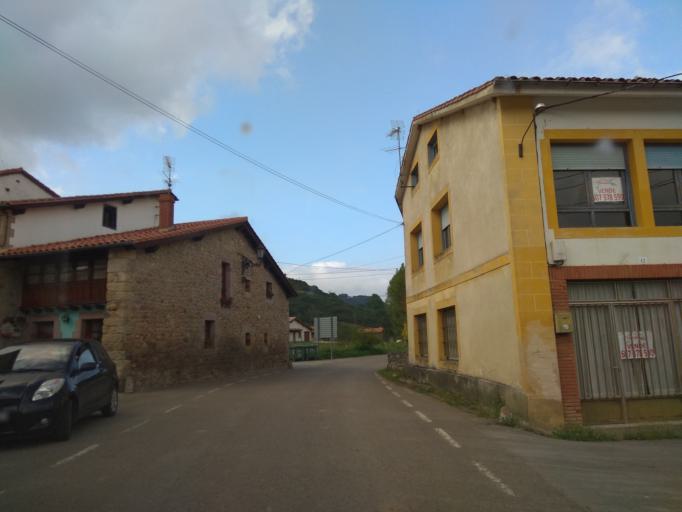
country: ES
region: Cantabria
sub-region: Provincia de Cantabria
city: San Vicente de la Barquera
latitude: 43.3196
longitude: -4.3516
